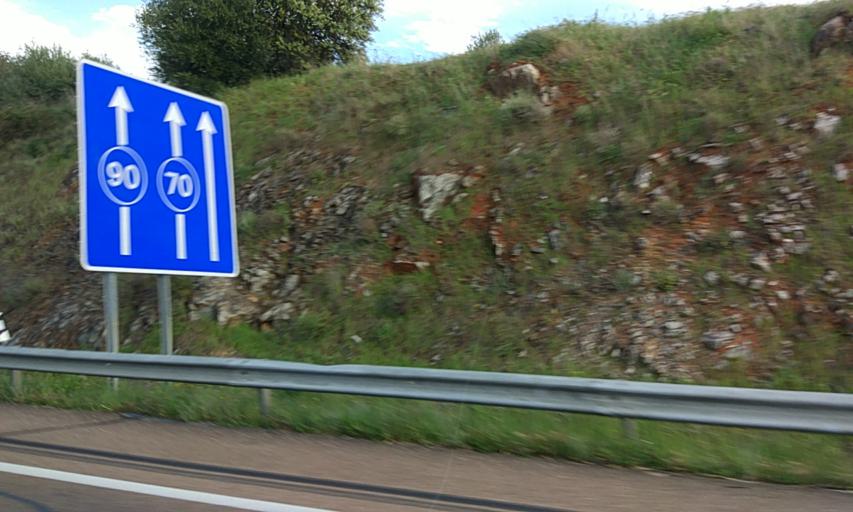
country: PT
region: Portalegre
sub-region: Elvas
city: Elvas
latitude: 38.9094
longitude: -7.1741
